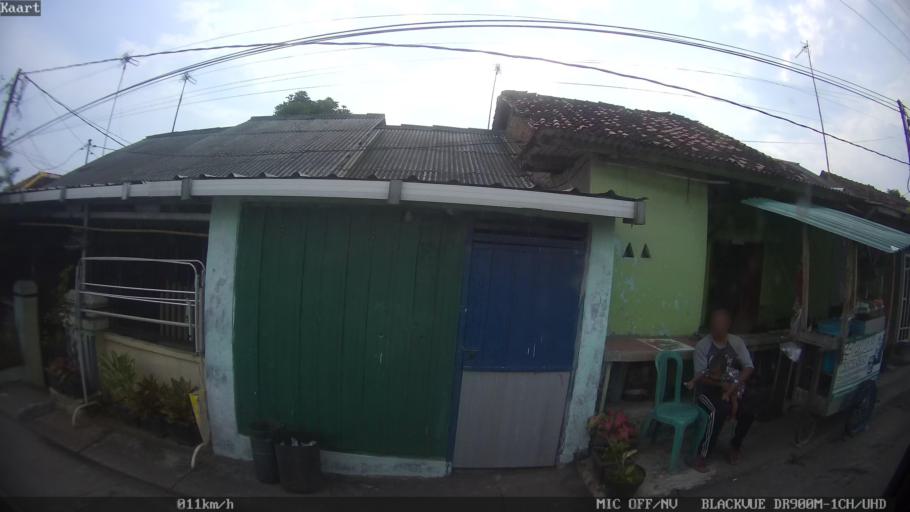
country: ID
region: Lampung
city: Bandarlampung
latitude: -5.4341
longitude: 105.2959
